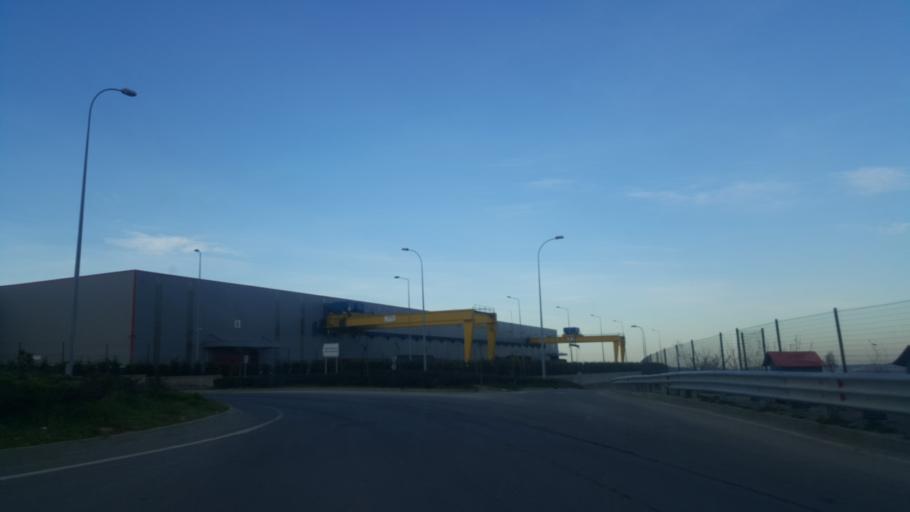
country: TR
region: Kocaeli
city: Tavsanli
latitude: 40.8380
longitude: 29.5499
